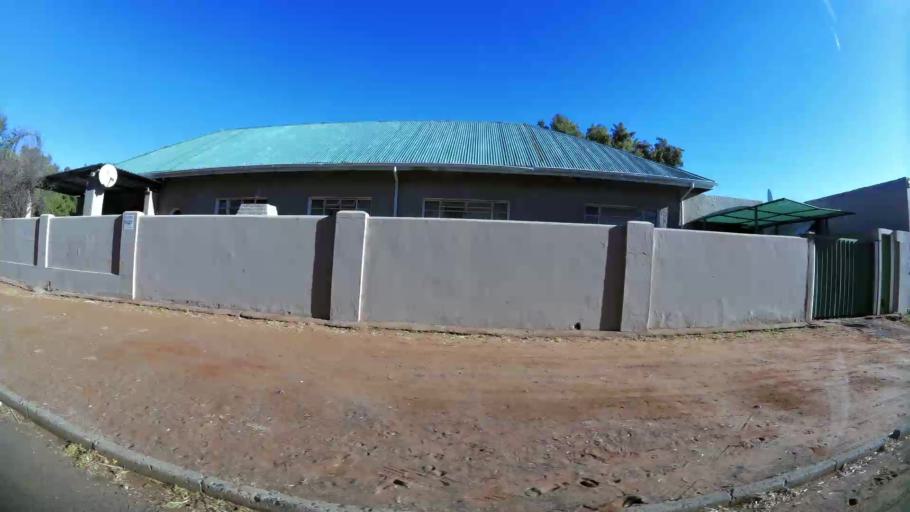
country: ZA
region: Northern Cape
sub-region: Frances Baard District Municipality
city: Kimberley
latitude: -28.7537
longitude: 24.7791
